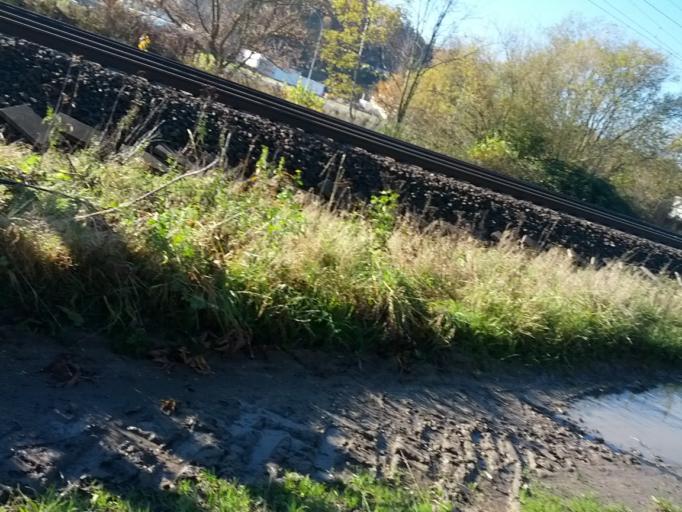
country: DE
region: Thuringia
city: Seebach
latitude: 50.9525
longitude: 10.4098
